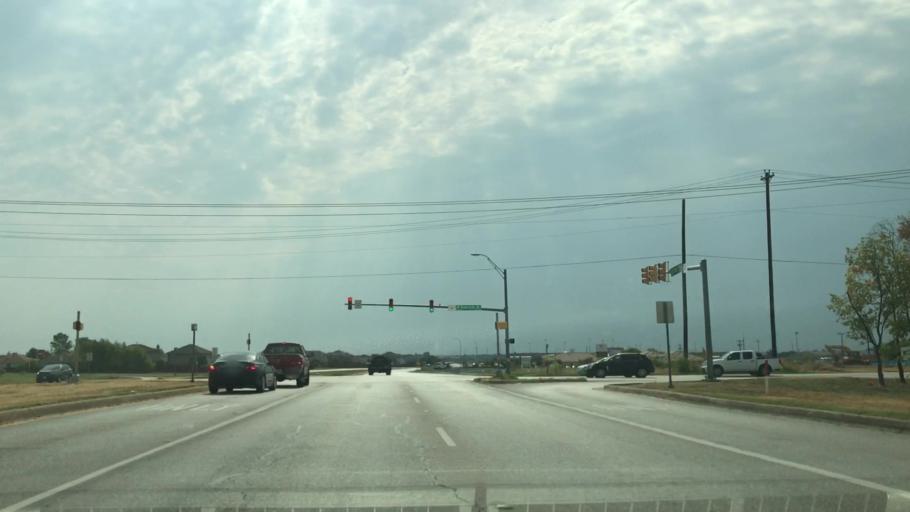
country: US
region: Texas
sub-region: Tarrant County
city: Blue Mound
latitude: 32.8958
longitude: -97.3075
